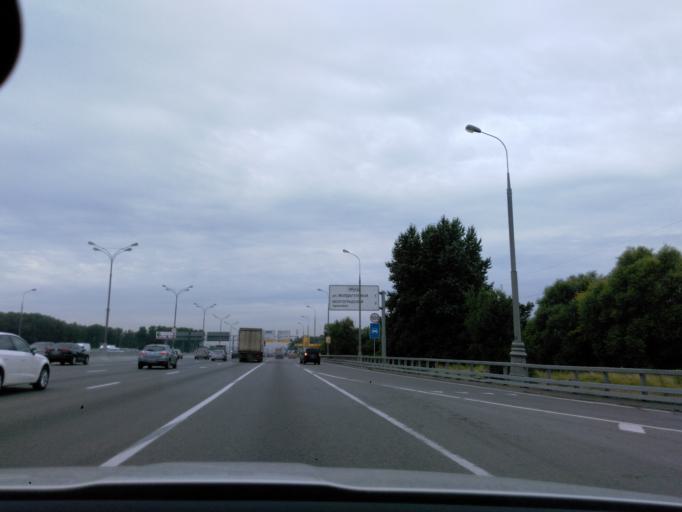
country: RU
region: Moskovskaya
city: Kuskovo
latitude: 55.7279
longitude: 37.8398
